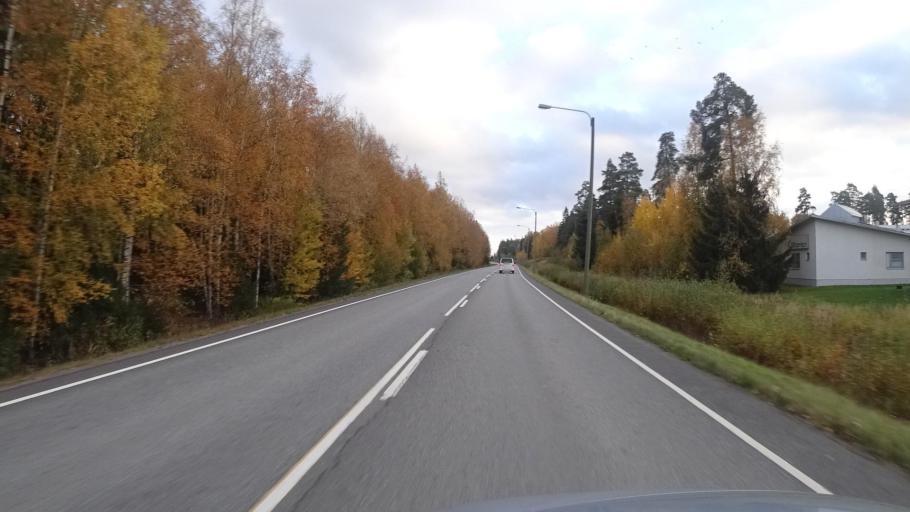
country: FI
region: Varsinais-Suomi
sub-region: Loimaa
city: Loimaa
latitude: 60.8775
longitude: 22.9925
